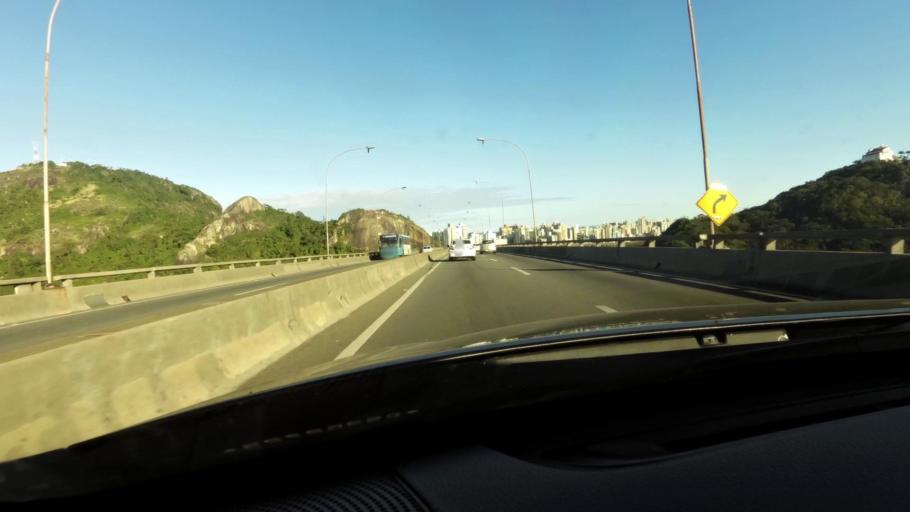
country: BR
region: Espirito Santo
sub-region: Vila Velha
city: Vila Velha
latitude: -20.3228
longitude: -40.2837
